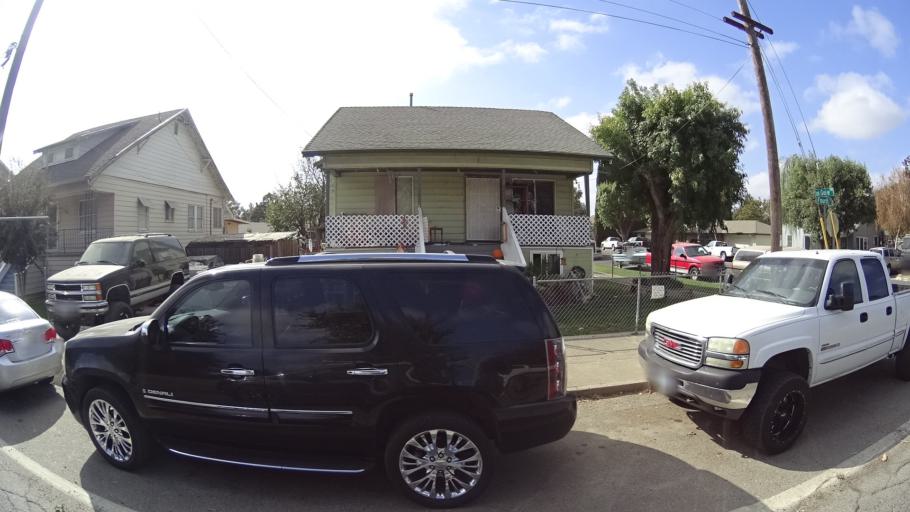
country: US
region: California
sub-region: Yolo County
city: Woodland
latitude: 38.8008
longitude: -121.7213
